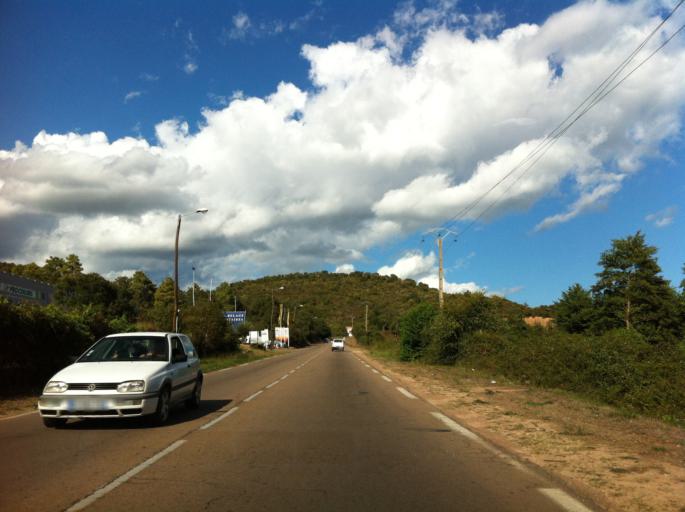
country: FR
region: Corsica
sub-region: Departement de la Corse-du-Sud
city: Porto-Vecchio
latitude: 41.6128
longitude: 9.2795
